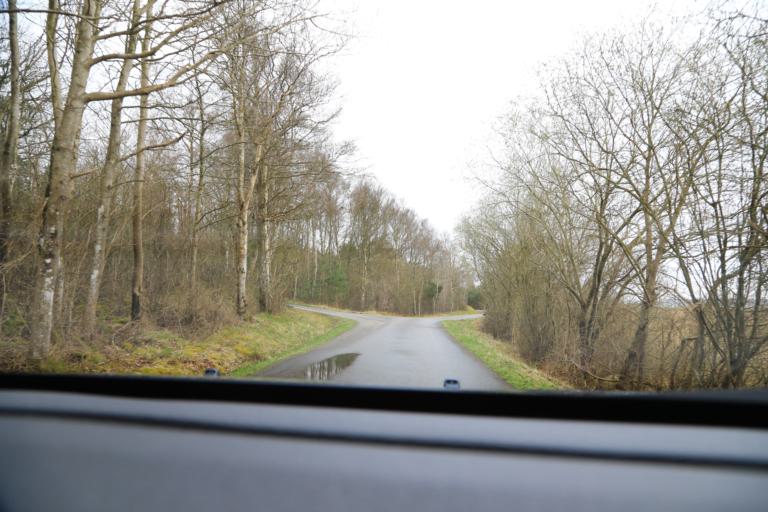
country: SE
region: Halland
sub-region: Kungsbacka Kommun
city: Frillesas
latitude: 57.3078
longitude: 12.1739
